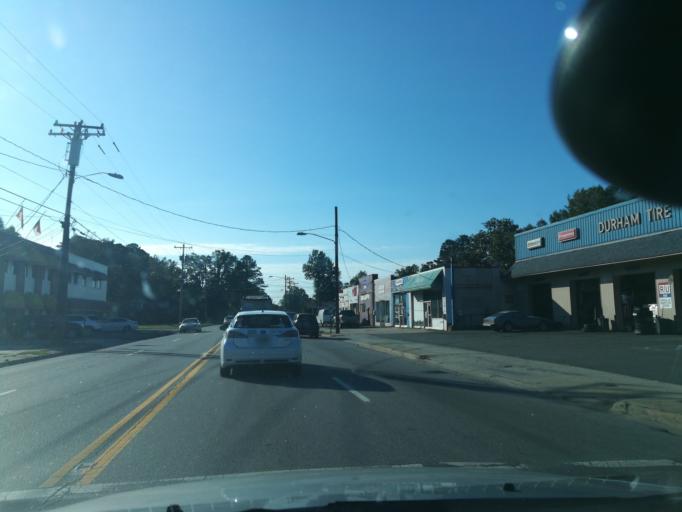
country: US
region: North Carolina
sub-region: Durham County
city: Durham
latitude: 36.0282
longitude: -78.8901
